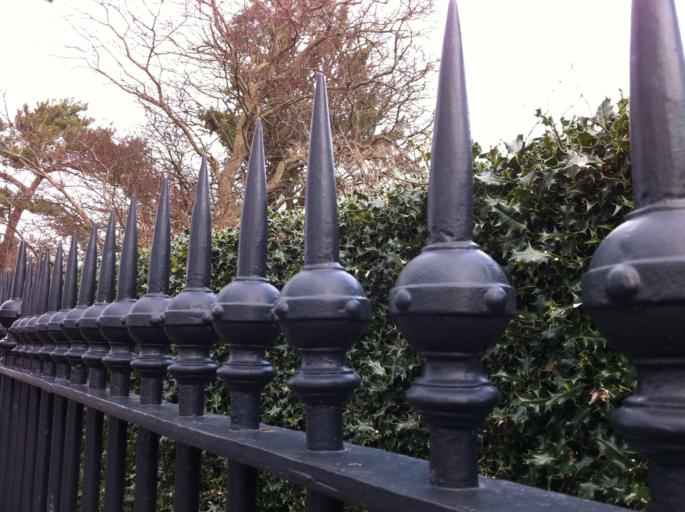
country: GB
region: Scotland
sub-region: Edinburgh
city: Edinburgh
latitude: 55.9630
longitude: -3.2117
